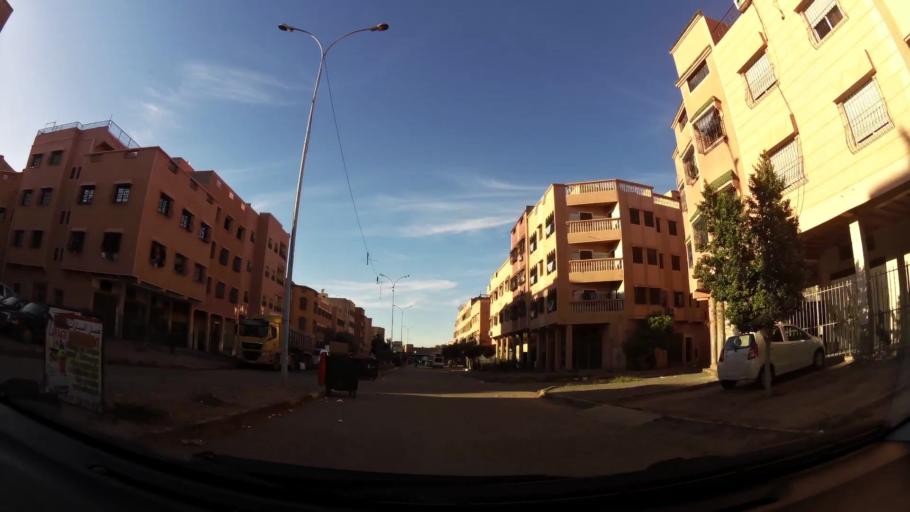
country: MA
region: Marrakech-Tensift-Al Haouz
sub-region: Marrakech
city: Marrakesh
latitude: 31.6149
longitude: -8.0586
